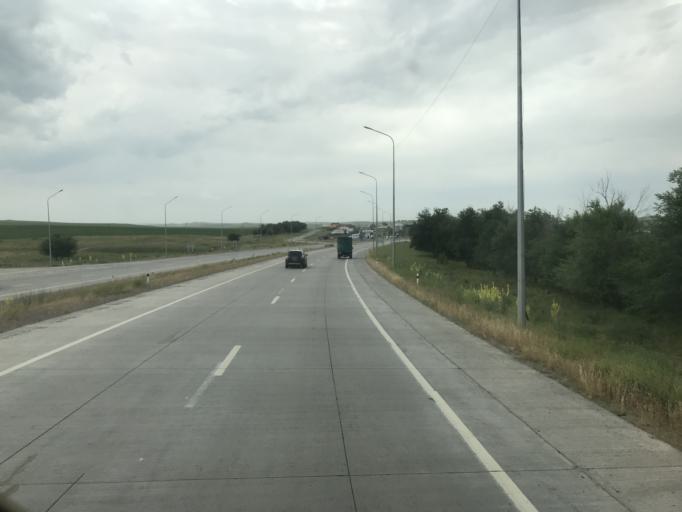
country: KZ
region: Ongtustik Qazaqstan
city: Shymkent
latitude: 42.2213
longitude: 69.5315
